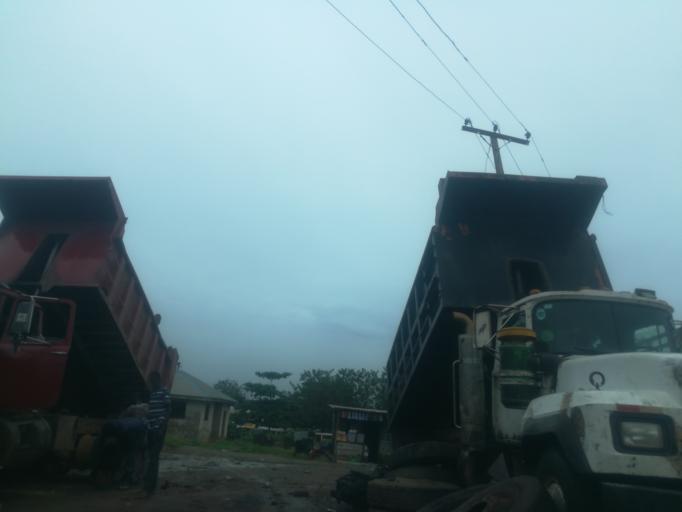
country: NG
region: Oyo
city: Ibadan
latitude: 7.3329
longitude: 3.8801
